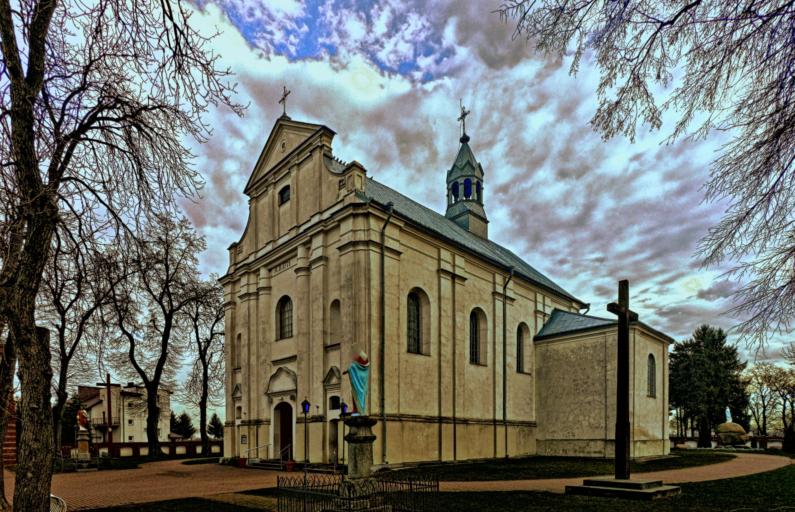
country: PL
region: Lublin Voivodeship
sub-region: Powiat radzynski
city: Borki
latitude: 51.8080
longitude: 22.4845
